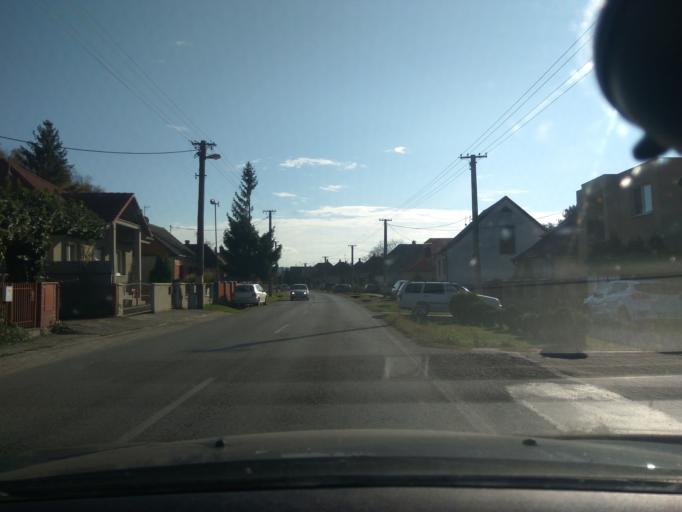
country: SK
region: Trnavsky
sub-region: Okres Trnava
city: Piestany
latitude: 48.5596
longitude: 17.8375
